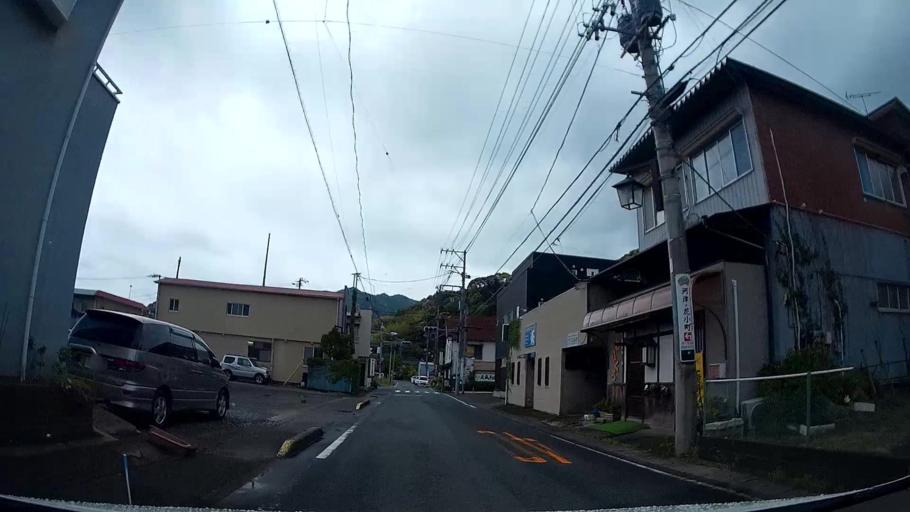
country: JP
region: Shizuoka
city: Shimoda
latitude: 34.7562
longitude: 138.9837
